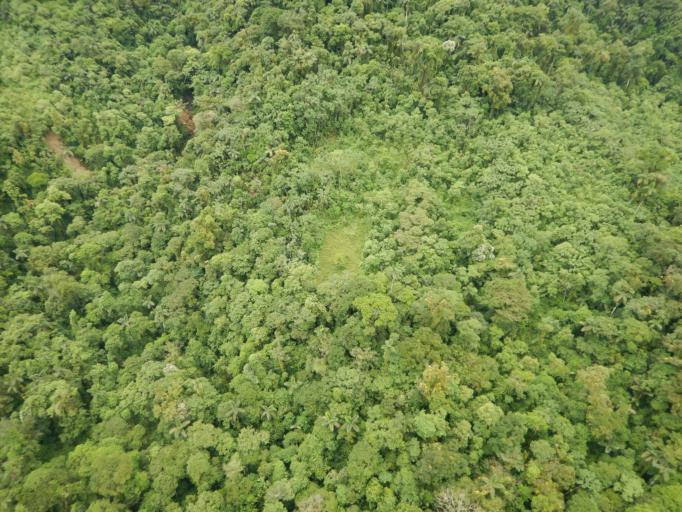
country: BO
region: Cochabamba
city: Chimore
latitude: -17.2230
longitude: -65.2664
